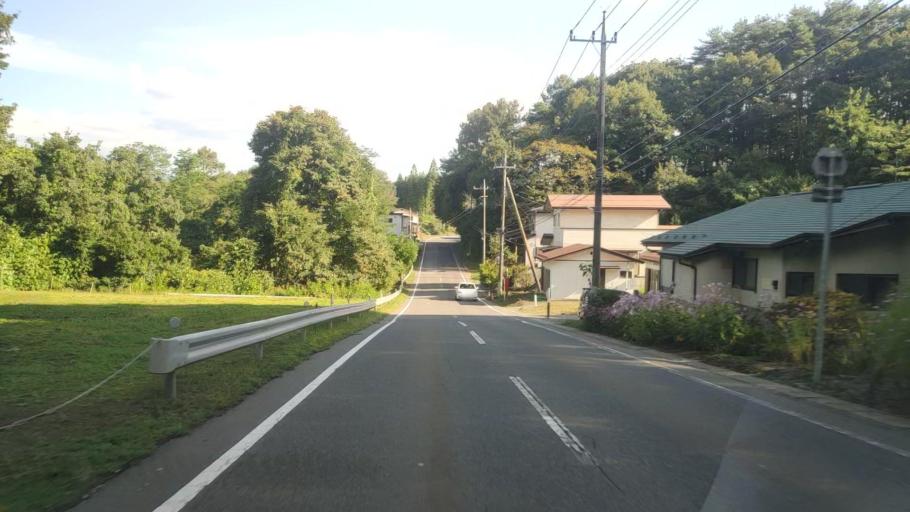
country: JP
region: Nagano
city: Komoro
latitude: 36.5444
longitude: 138.5555
